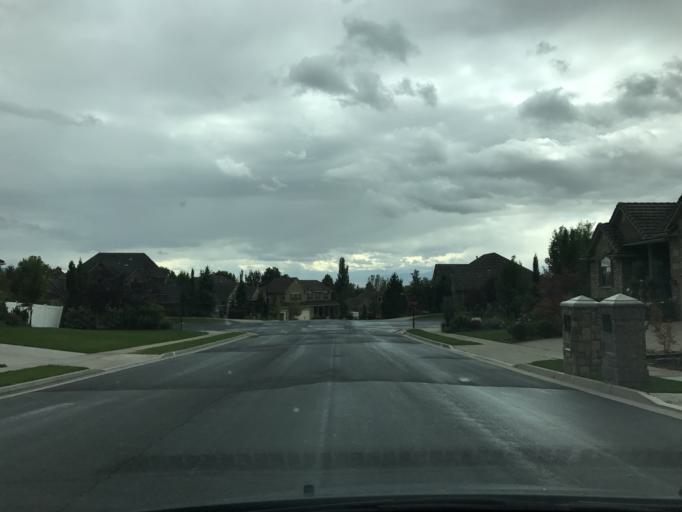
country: US
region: Utah
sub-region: Davis County
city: Fruit Heights
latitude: 41.0178
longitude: -111.9071
